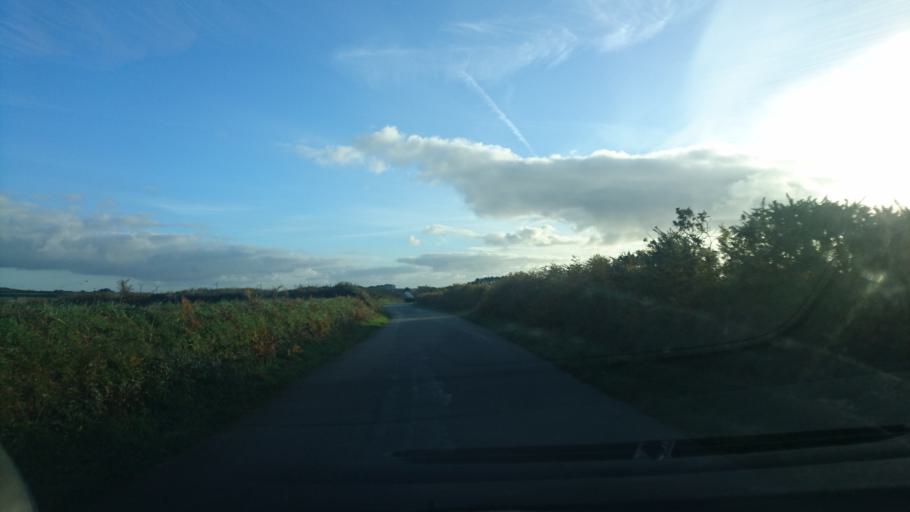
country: FR
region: Brittany
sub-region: Departement du Finistere
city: Lampaul-Plouarzel
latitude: 48.4293
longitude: -4.7694
